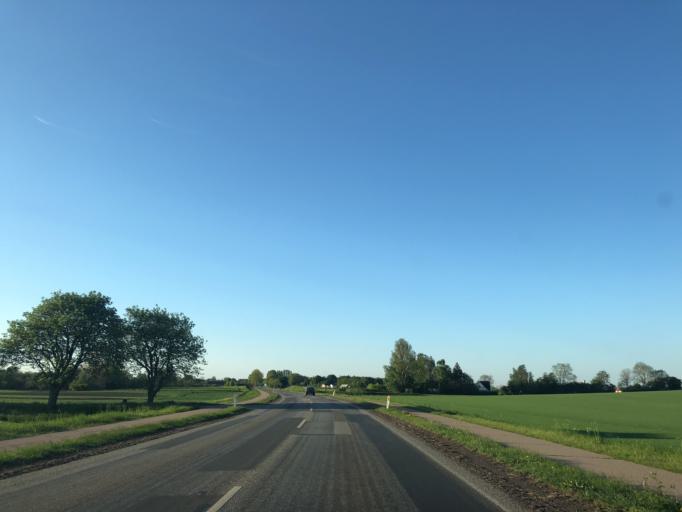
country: DK
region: Zealand
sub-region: Stevns Kommune
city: Harlev
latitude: 55.3665
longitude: 12.2555
